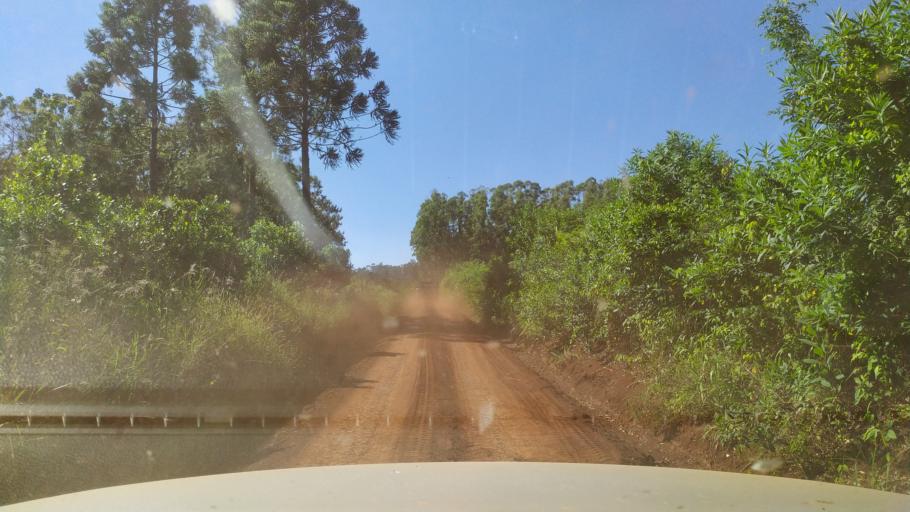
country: AR
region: Misiones
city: Caraguatay
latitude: -26.6709
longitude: -54.6978
